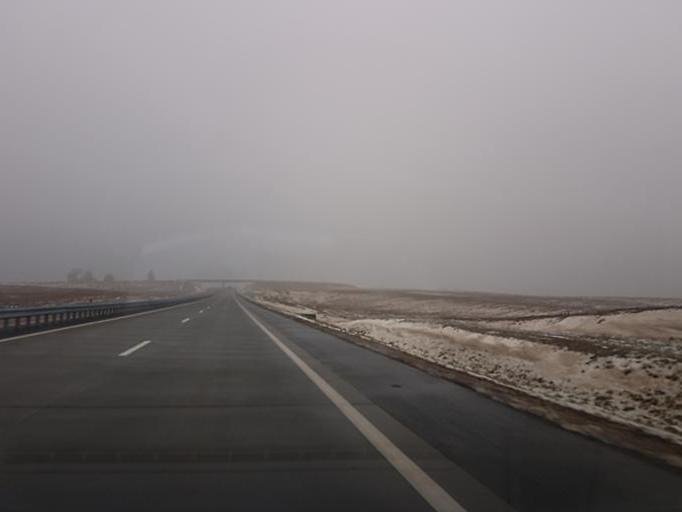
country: BY
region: Minsk
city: Atolina
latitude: 53.7278
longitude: 27.4251
